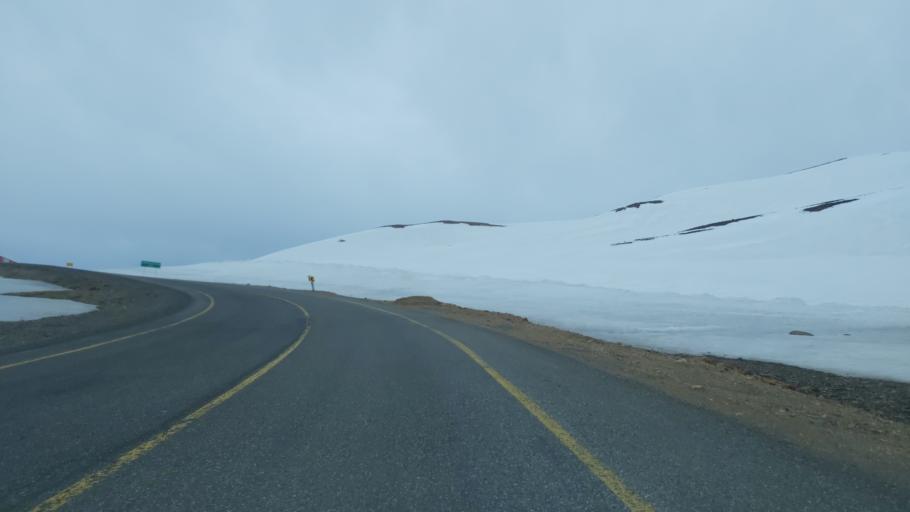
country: CL
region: Maule
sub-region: Provincia de Linares
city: Colbun
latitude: -36.0070
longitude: -70.4791
